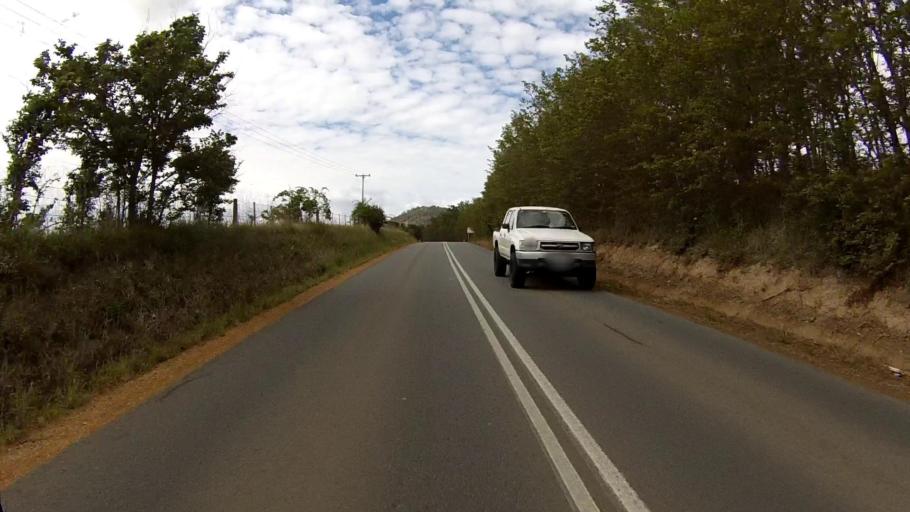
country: AU
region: Tasmania
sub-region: Clarence
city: Cambridge
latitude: -42.8049
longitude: 147.4232
